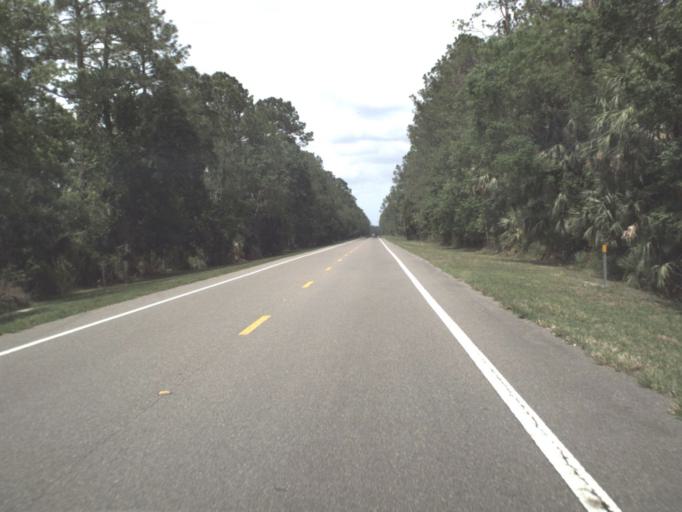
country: US
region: Florida
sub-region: Flagler County
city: Bunnell
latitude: 29.3907
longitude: -81.3085
